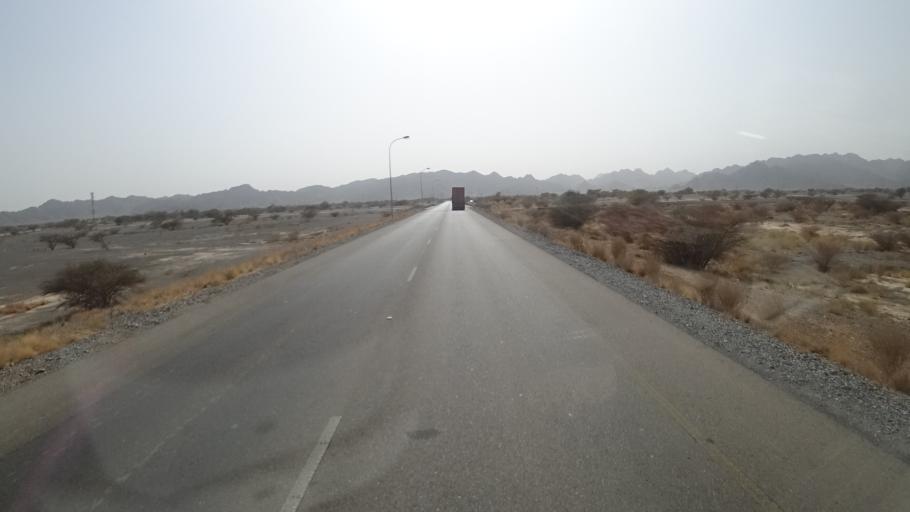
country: OM
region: Muhafazat ad Dakhiliyah
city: Nizwa
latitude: 22.9969
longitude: 57.5472
